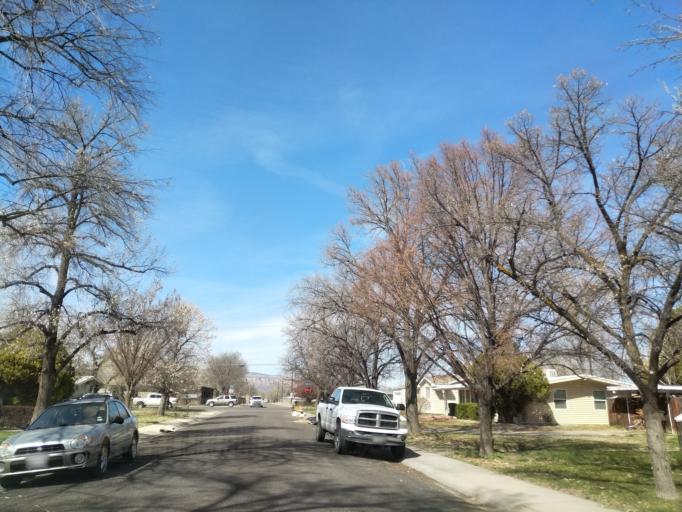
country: US
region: Colorado
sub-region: Mesa County
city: Grand Junction
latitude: 39.0828
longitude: -108.5699
